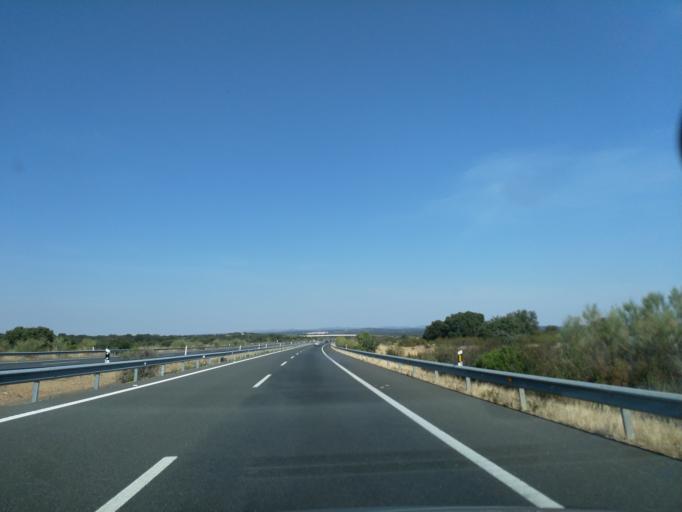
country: ES
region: Extremadura
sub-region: Provincia de Caceres
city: Alcuescar
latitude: 39.1840
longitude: -6.2754
